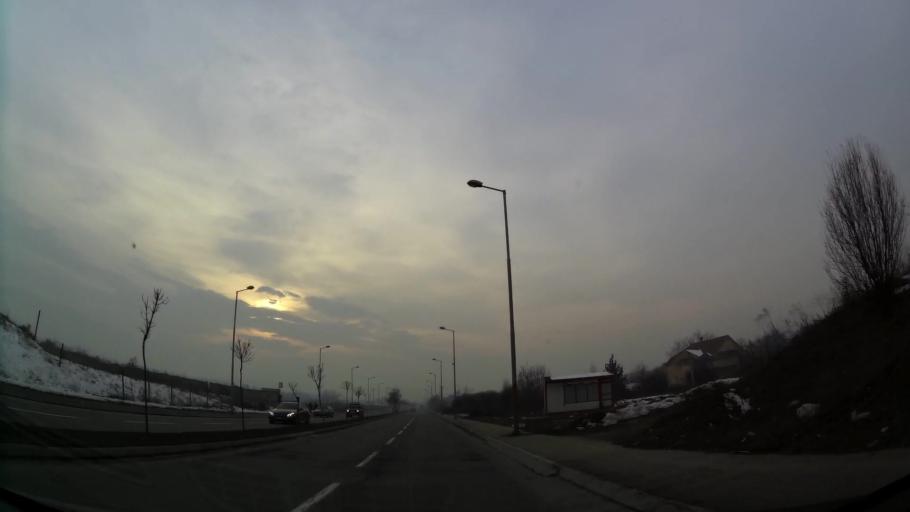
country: MK
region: Suto Orizari
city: Suto Orizare
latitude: 42.0270
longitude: 21.4184
